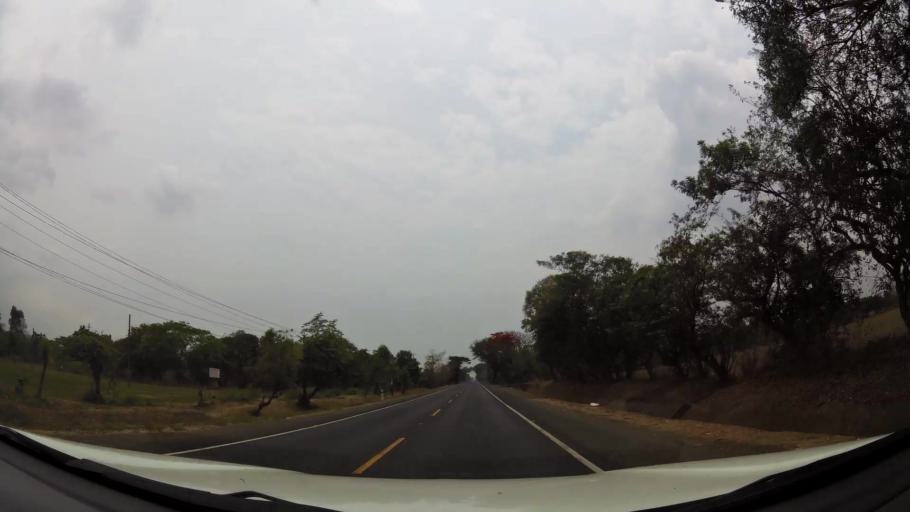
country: NI
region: Leon
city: Quezalguaque
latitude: 12.5390
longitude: -86.9090
